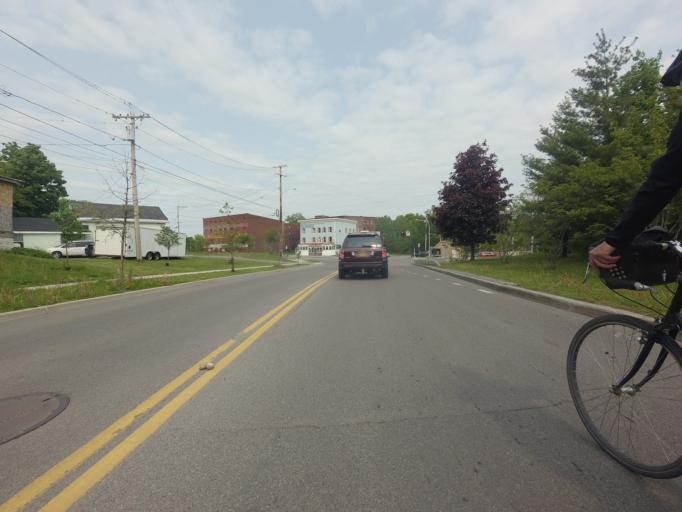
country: US
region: New York
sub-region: Jefferson County
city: Watertown
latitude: 43.9777
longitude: -75.8980
